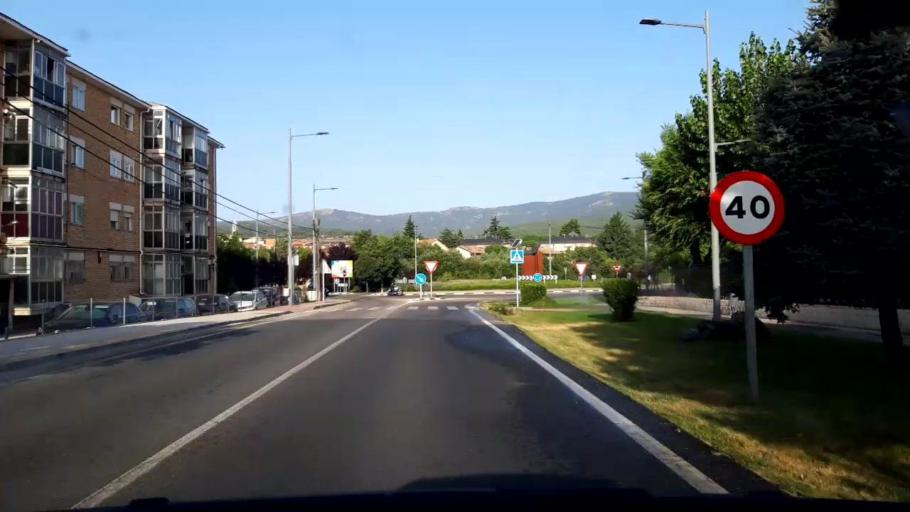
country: ES
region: Madrid
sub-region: Provincia de Madrid
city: Guadarrama
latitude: 40.6759
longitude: -4.0816
